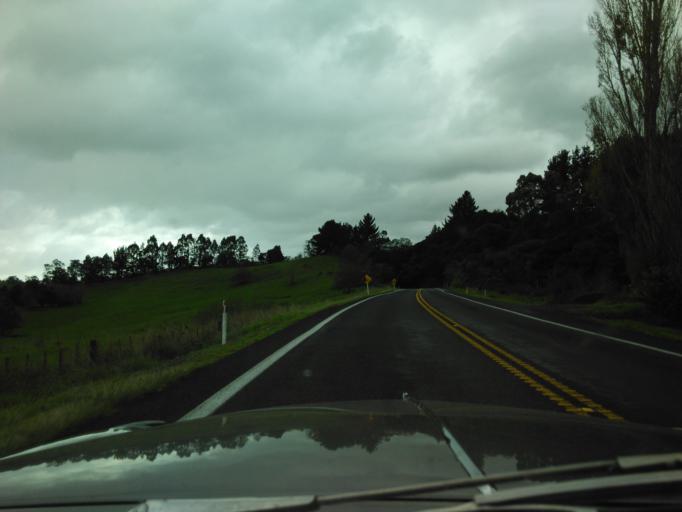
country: NZ
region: Waikato
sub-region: Hauraki District
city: Paeroa
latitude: -37.3966
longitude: 175.6932
